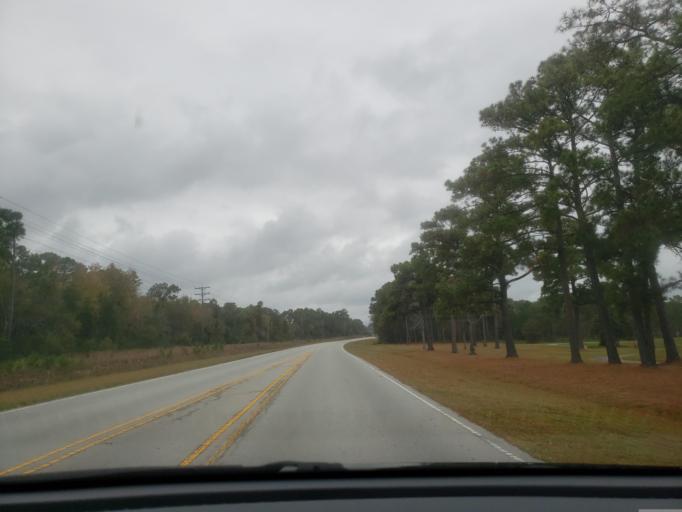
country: US
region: North Carolina
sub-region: Onslow County
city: Sneads Ferry
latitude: 34.5113
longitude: -77.4346
